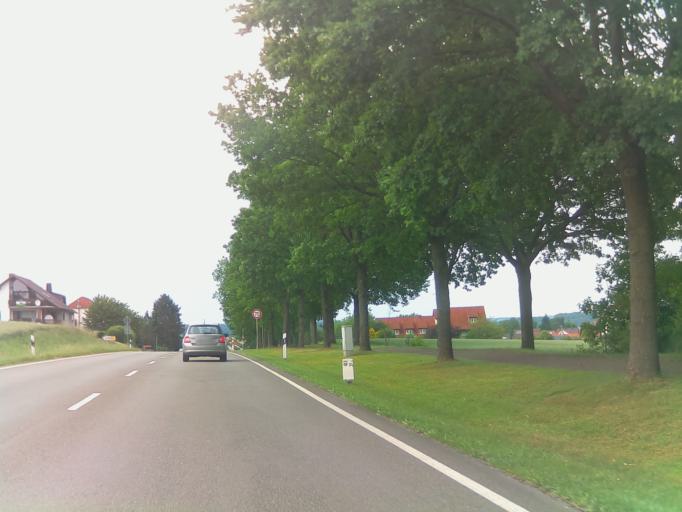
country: DE
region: Hesse
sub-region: Regierungsbezirk Kassel
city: Bad Arolsen
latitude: 51.3760
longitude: 9.0560
